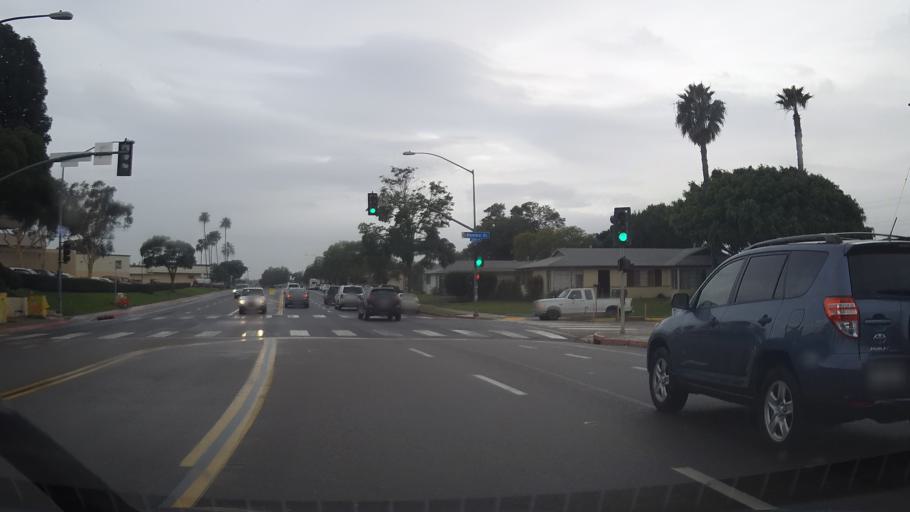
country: US
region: California
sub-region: San Diego County
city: La Jolla
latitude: 32.8332
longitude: -117.2026
